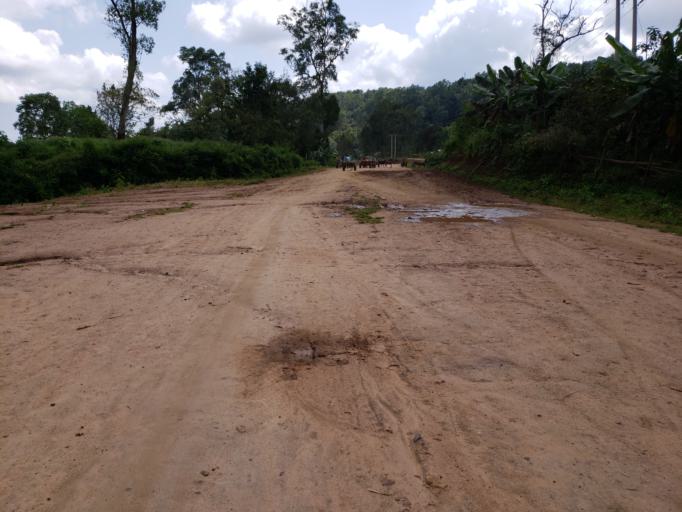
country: ET
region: Oromiya
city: Dodola
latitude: 6.4559
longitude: 39.5696
